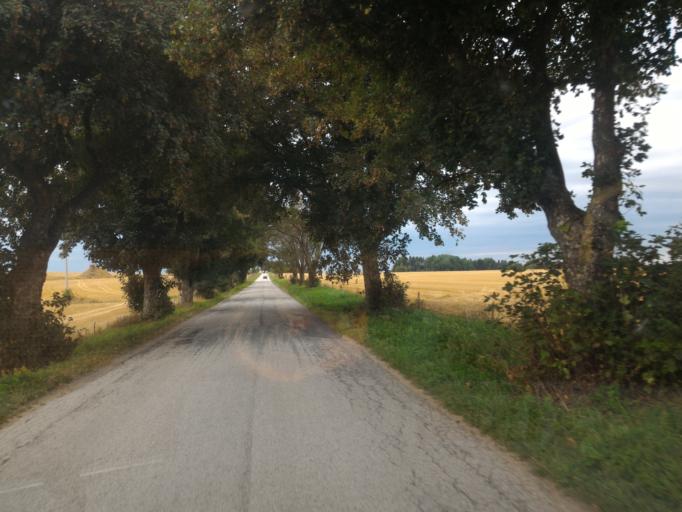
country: CZ
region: Vysocina
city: Knezice
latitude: 49.2407
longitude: 15.5754
